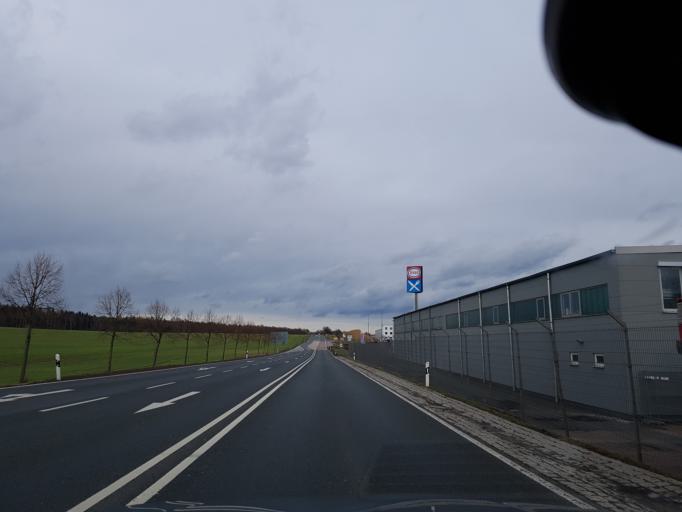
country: DE
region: Saxony
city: Hainichen
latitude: 50.9853
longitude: 13.1090
